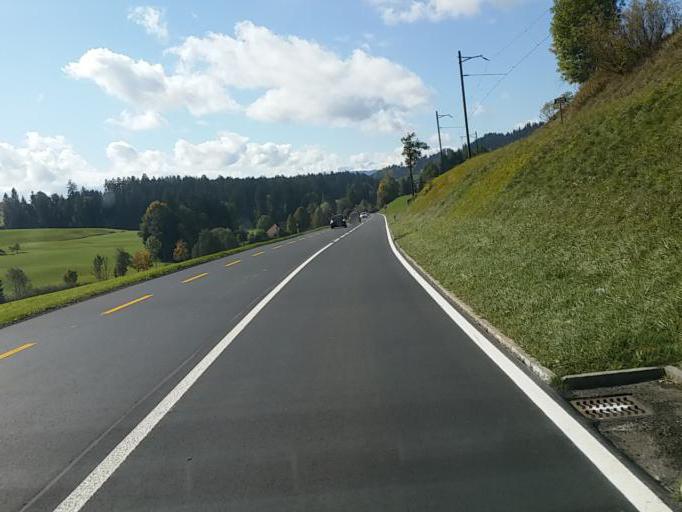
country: CH
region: Bern
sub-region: Emmental District
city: Sumiswald
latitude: 47.0498
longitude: 7.7483
